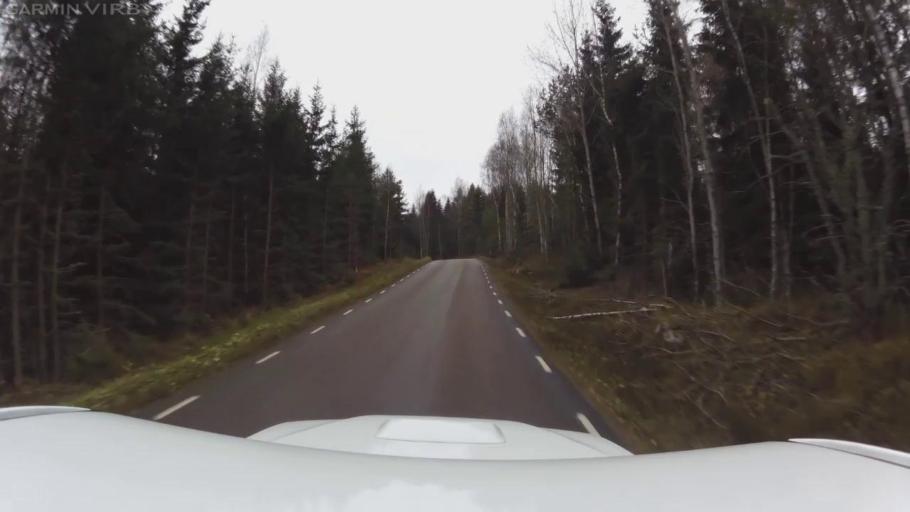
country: SE
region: OEstergoetland
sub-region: Mjolby Kommun
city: Mantorp
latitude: 58.1618
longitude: 15.3936
